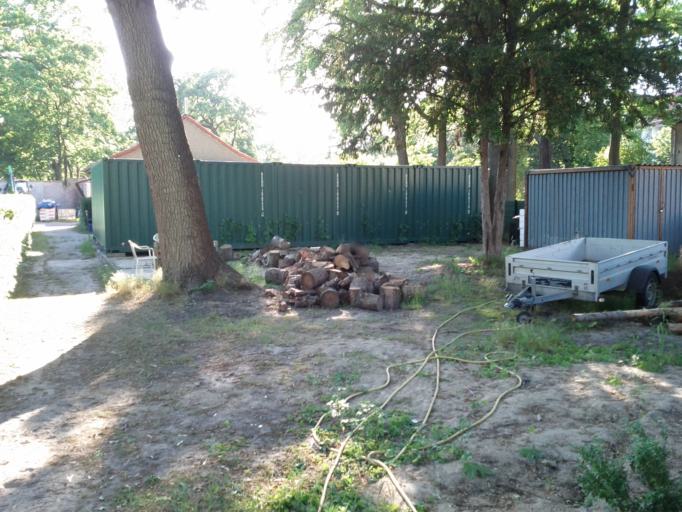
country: DE
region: Berlin
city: Kopenick Bezirk
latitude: 52.4437
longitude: 13.5664
